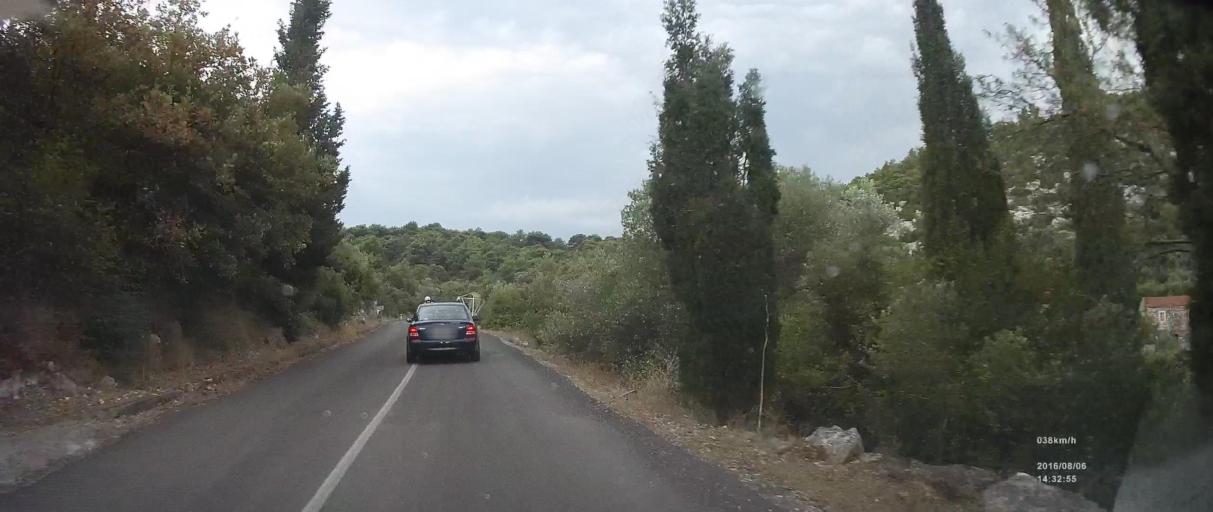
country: HR
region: Dubrovacko-Neretvanska
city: Ston
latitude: 42.7101
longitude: 17.7075
